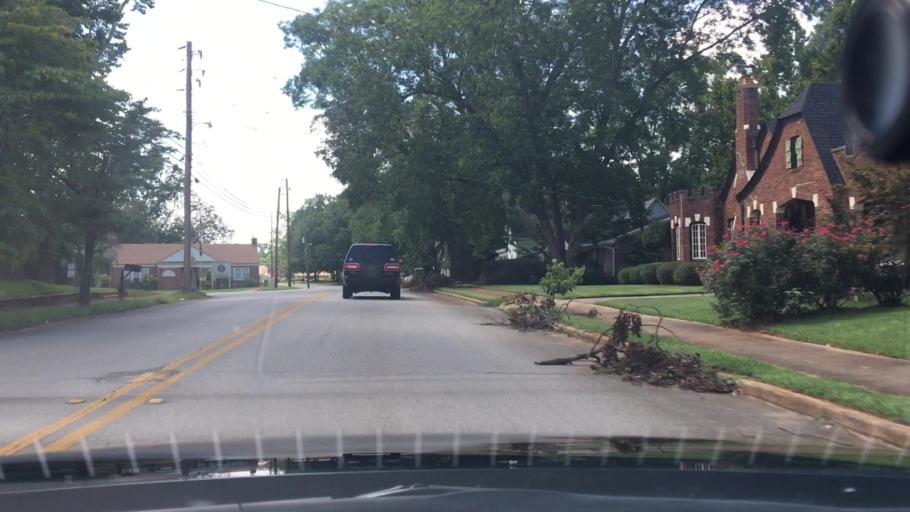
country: US
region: Georgia
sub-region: Jasper County
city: Monticello
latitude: 33.3021
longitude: -83.6787
